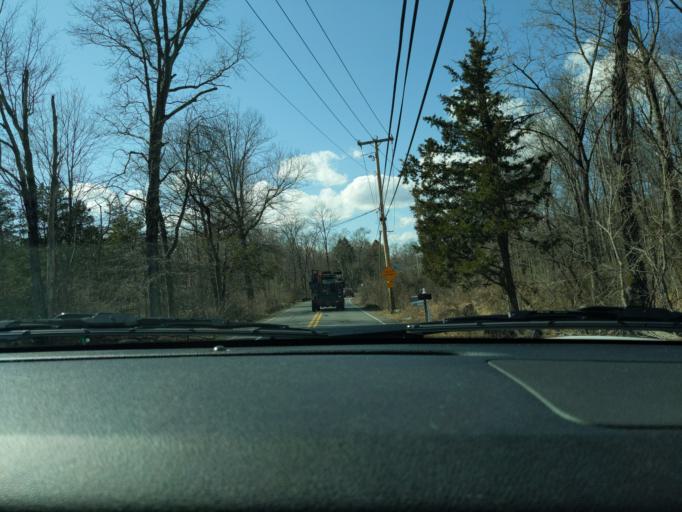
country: US
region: Pennsylvania
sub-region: Bucks County
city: Richlandtown
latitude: 40.4520
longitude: -75.2574
